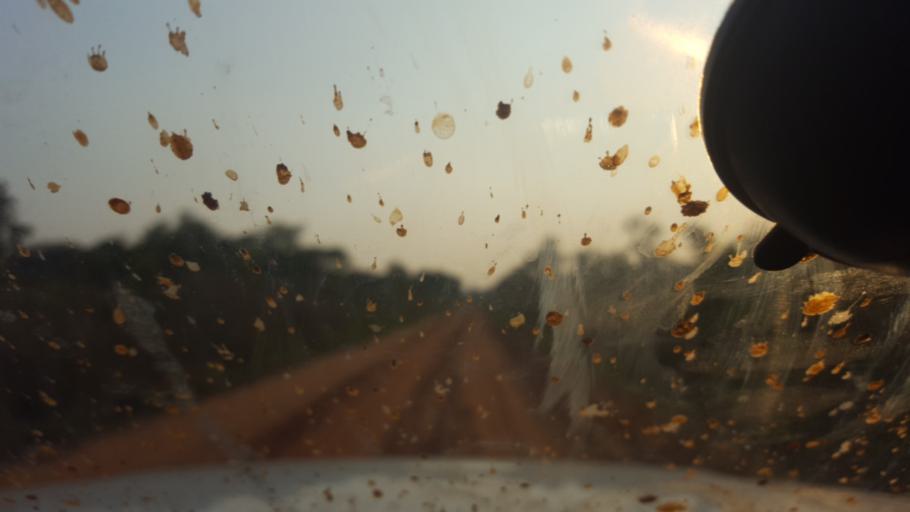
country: CD
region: Bandundu
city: Mushie
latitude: -3.7517
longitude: 16.6743
